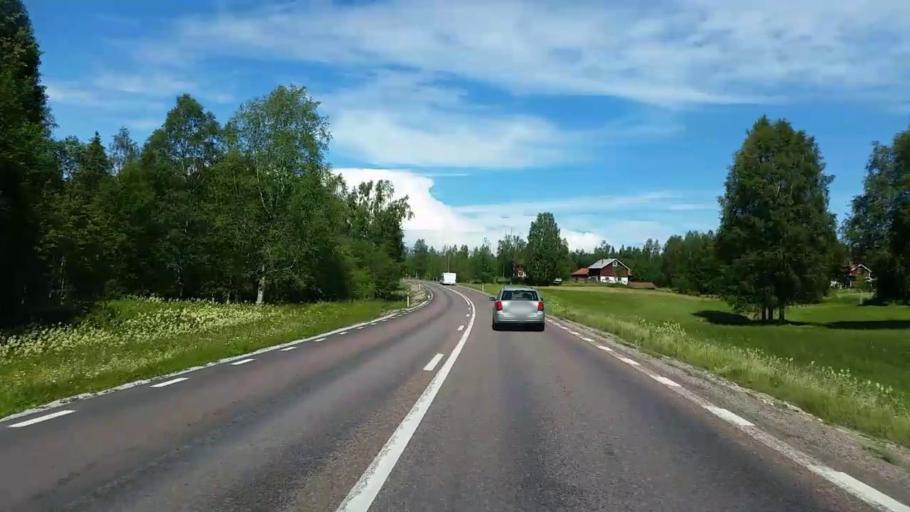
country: SE
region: Dalarna
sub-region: Rattviks Kommun
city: Raettvik
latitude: 60.9770
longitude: 15.2247
